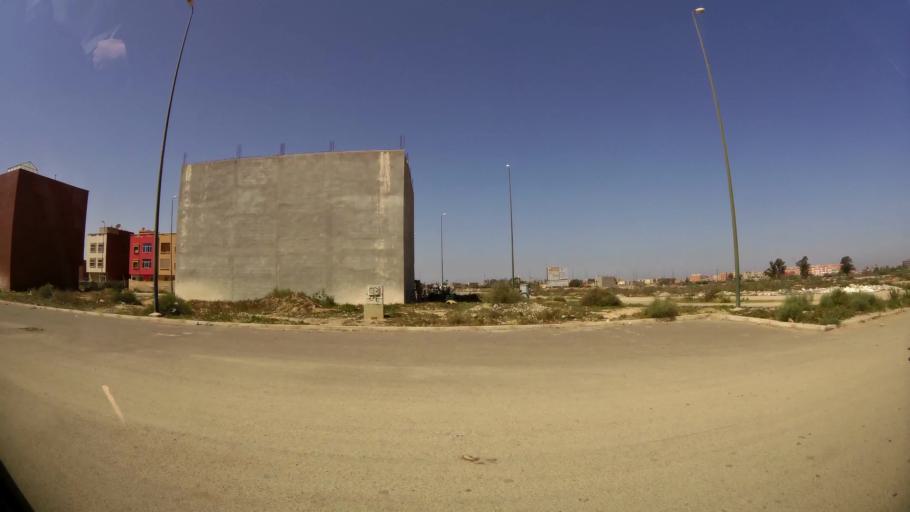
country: MA
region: Souss-Massa-Draa
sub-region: Inezgane-Ait Mellou
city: Inezgane
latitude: 30.3341
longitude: -9.5102
